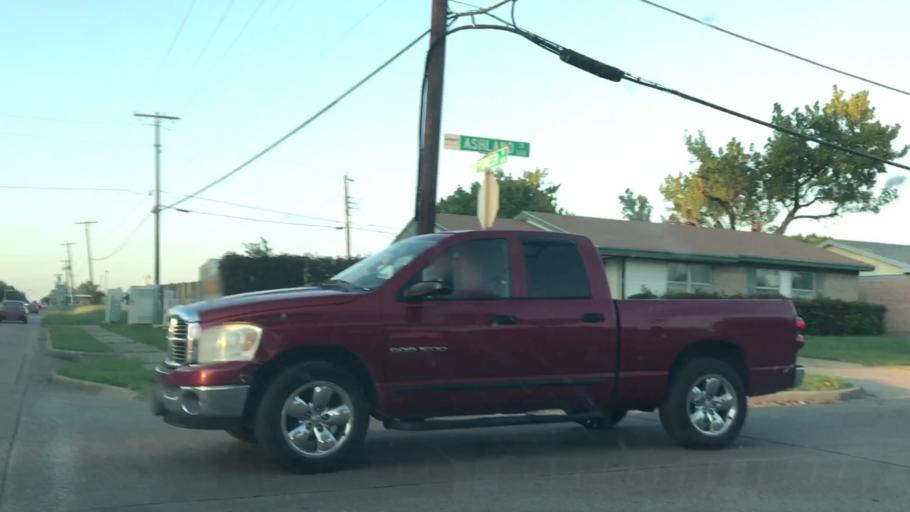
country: US
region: Texas
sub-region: Dallas County
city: Mesquite
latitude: 32.7489
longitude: -96.5834
